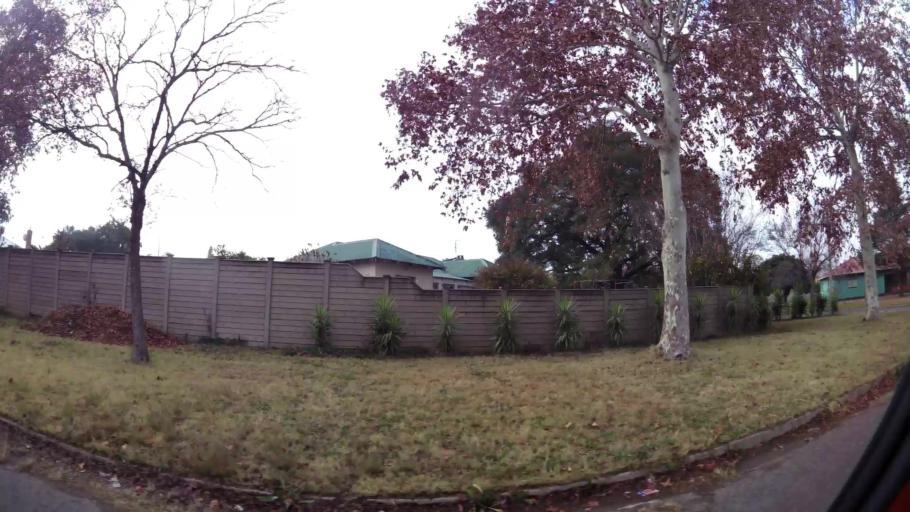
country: ZA
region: Gauteng
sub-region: Sedibeng District Municipality
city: Vanderbijlpark
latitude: -26.6857
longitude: 27.8159
